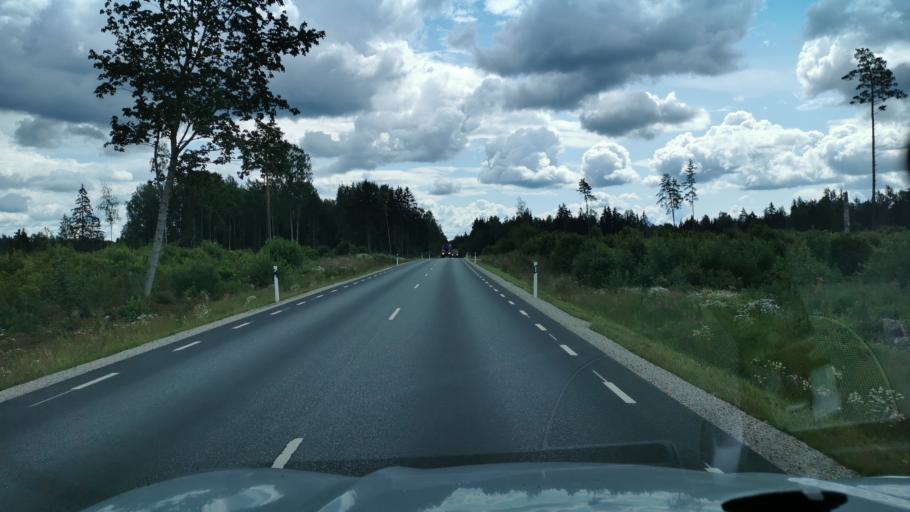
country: EE
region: Harju
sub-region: Raasiku vald
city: Raasiku
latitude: 59.2928
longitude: 25.1813
